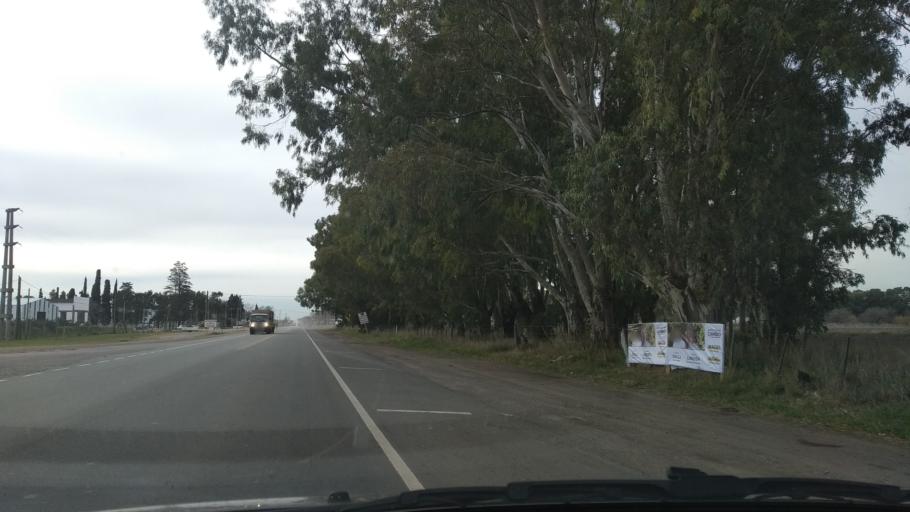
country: AR
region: Buenos Aires
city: Olavarria
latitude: -36.9647
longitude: -60.2654
